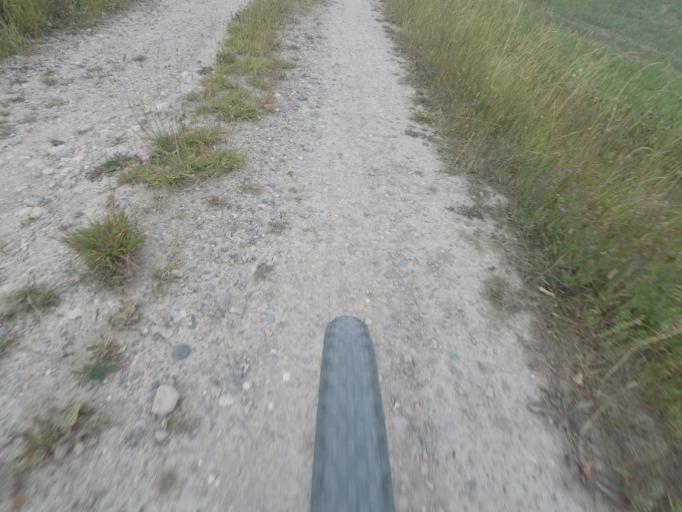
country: SE
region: Soedermanland
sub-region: Eskilstuna Kommun
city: Kvicksund
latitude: 59.4286
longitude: 16.2894
